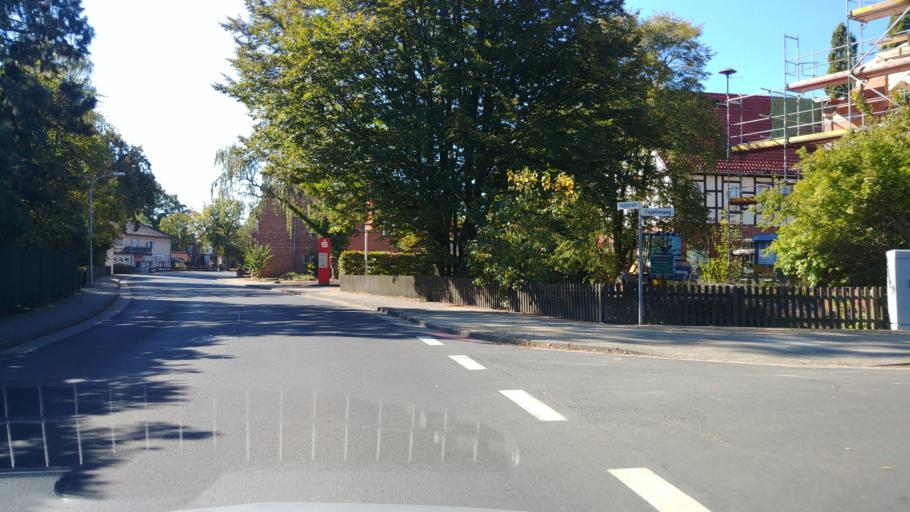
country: DE
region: Lower Saxony
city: Hillerse
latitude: 52.4125
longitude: 10.4026
